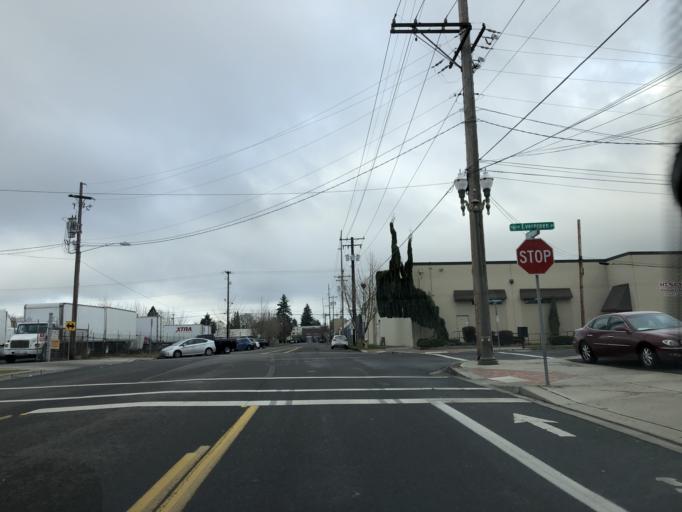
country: US
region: Washington
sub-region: Clark County
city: Vancouver
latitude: 45.6286
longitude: -122.6814
